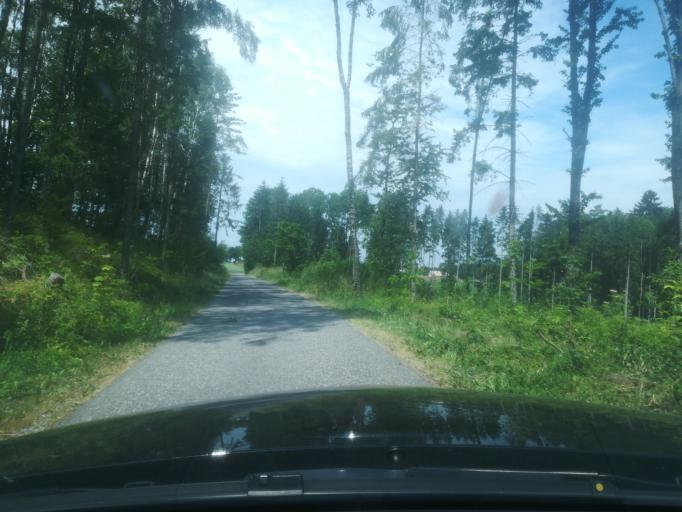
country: AT
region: Upper Austria
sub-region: Politischer Bezirk Urfahr-Umgebung
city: Herzogsdorf
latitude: 48.3949
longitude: 14.0883
